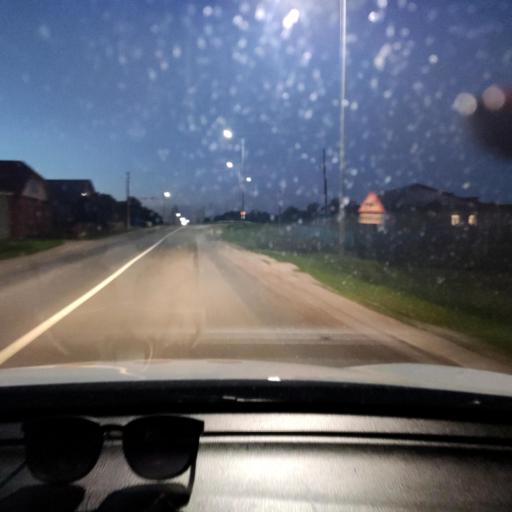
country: RU
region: Tatarstan
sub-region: Alekseyevskiy Rayon
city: Alekseyevskoye
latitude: 55.4258
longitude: 49.8787
